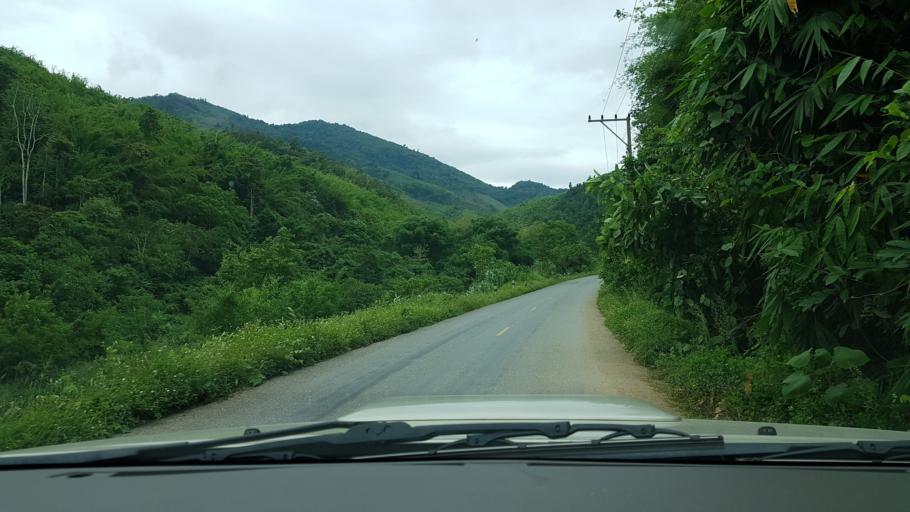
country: LA
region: Oudomxai
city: Muang La
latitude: 20.9265
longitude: 102.2051
